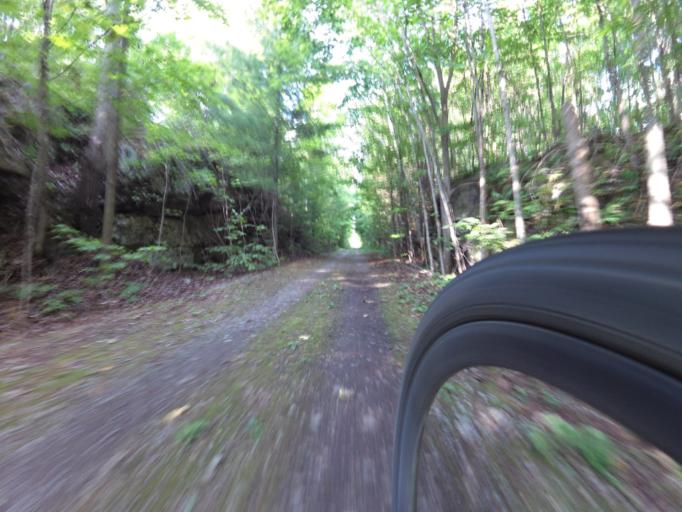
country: CA
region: Ontario
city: Kingston
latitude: 44.4363
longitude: -76.5360
